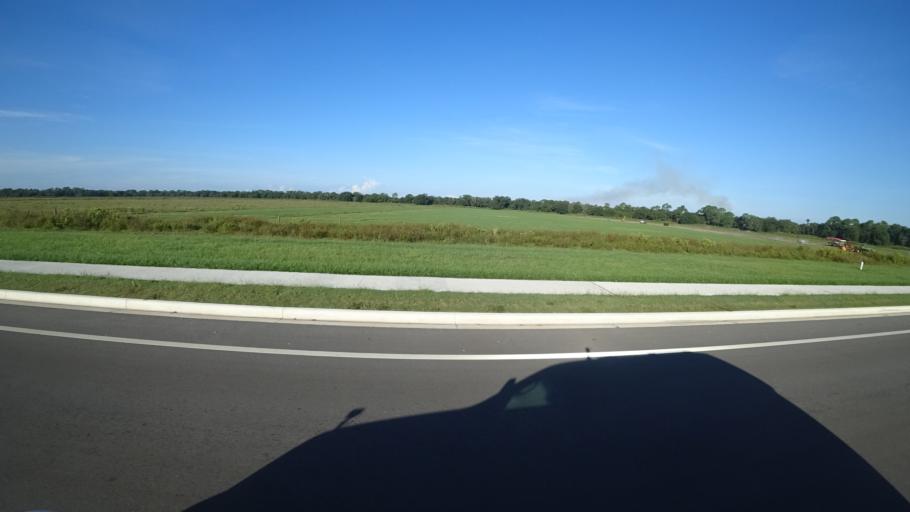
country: US
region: Florida
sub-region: Sarasota County
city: The Meadows
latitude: 27.4401
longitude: -82.3712
